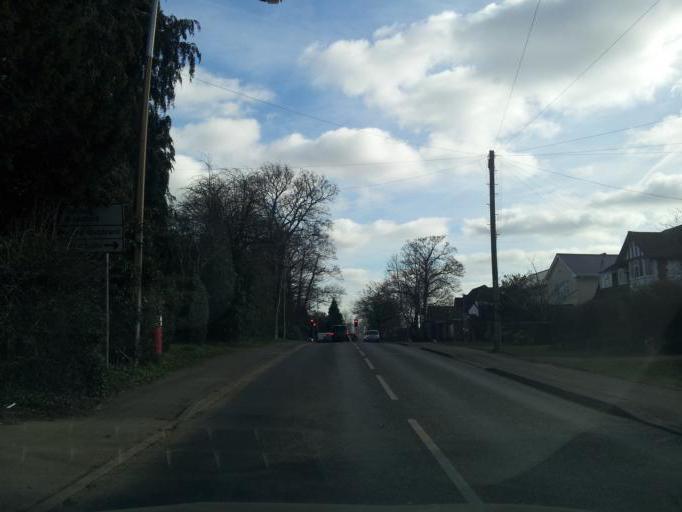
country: GB
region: England
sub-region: Hertfordshire
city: St Albans
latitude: 51.7597
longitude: -0.3089
